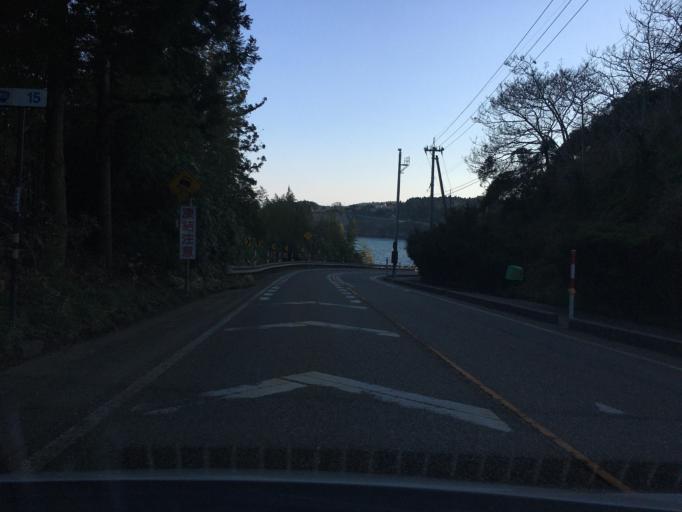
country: JP
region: Ishikawa
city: Nanao
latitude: 36.9914
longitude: 137.0526
